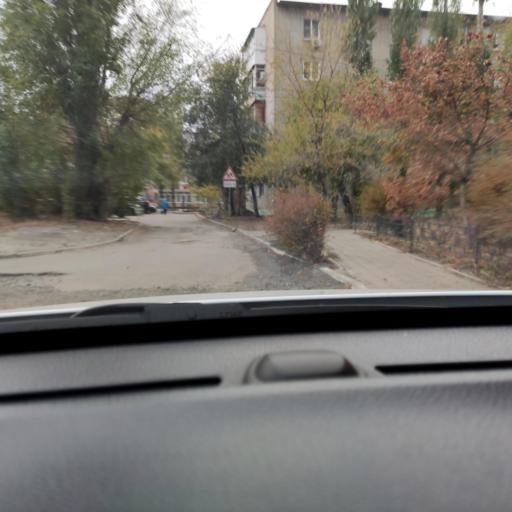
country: RU
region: Voronezj
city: Voronezh
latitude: 51.6908
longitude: 39.2572
